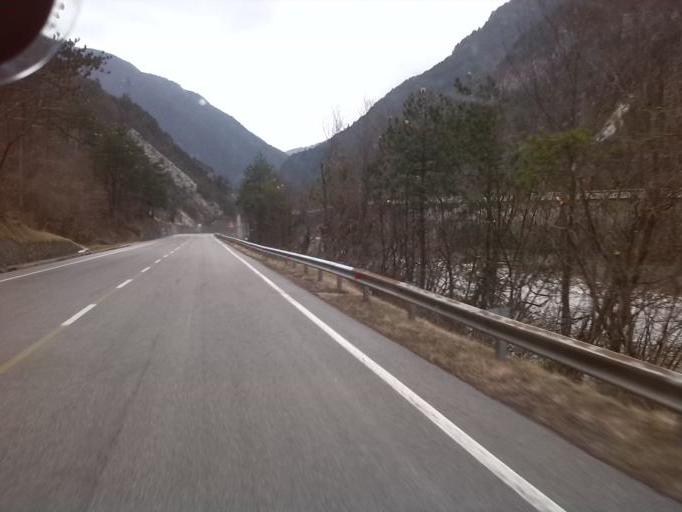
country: IT
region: Friuli Venezia Giulia
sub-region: Provincia di Udine
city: Dogna
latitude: 46.4266
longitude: 13.3162
